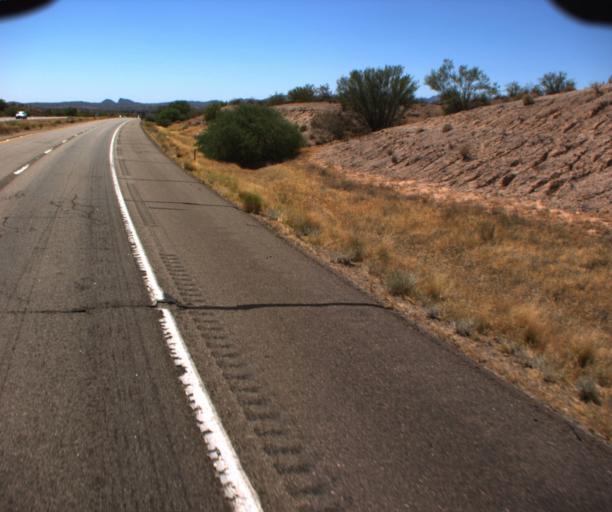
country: US
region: Arizona
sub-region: Maricopa County
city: Fountain Hills
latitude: 33.5811
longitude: -111.6252
